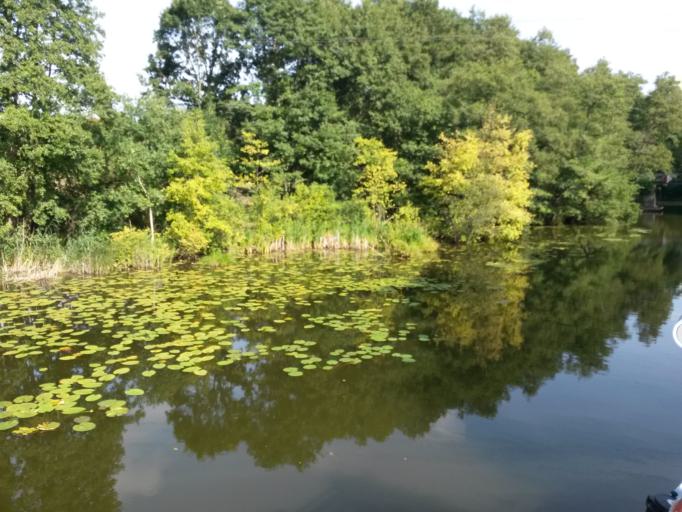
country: DE
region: Brandenburg
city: Templin
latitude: 53.1386
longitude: 13.5414
